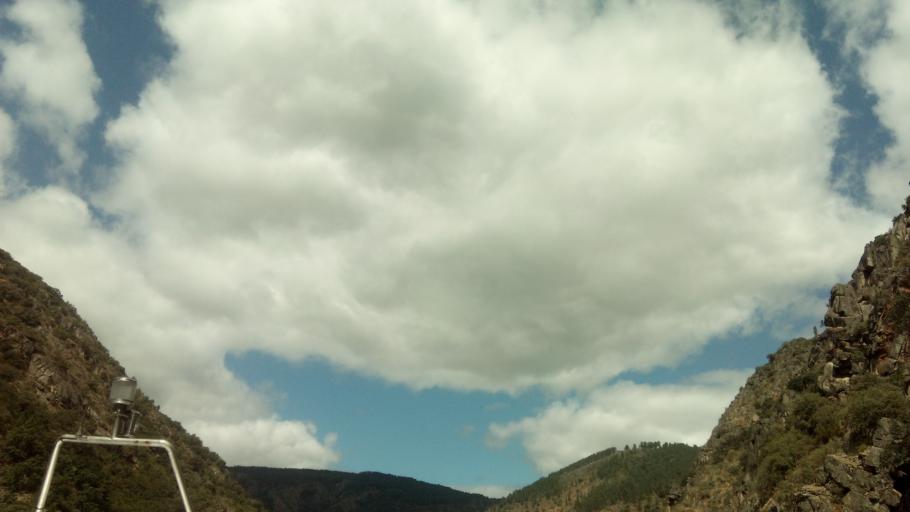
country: ES
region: Galicia
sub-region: Provincia de Lugo
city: Lobios
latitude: 42.3950
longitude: -7.5590
